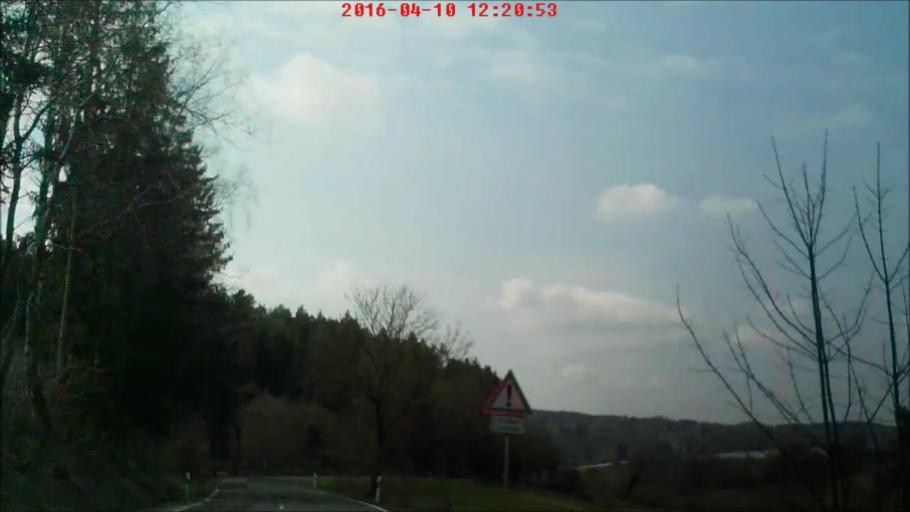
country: DE
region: Thuringia
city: Viernau
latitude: 50.6569
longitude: 10.5787
